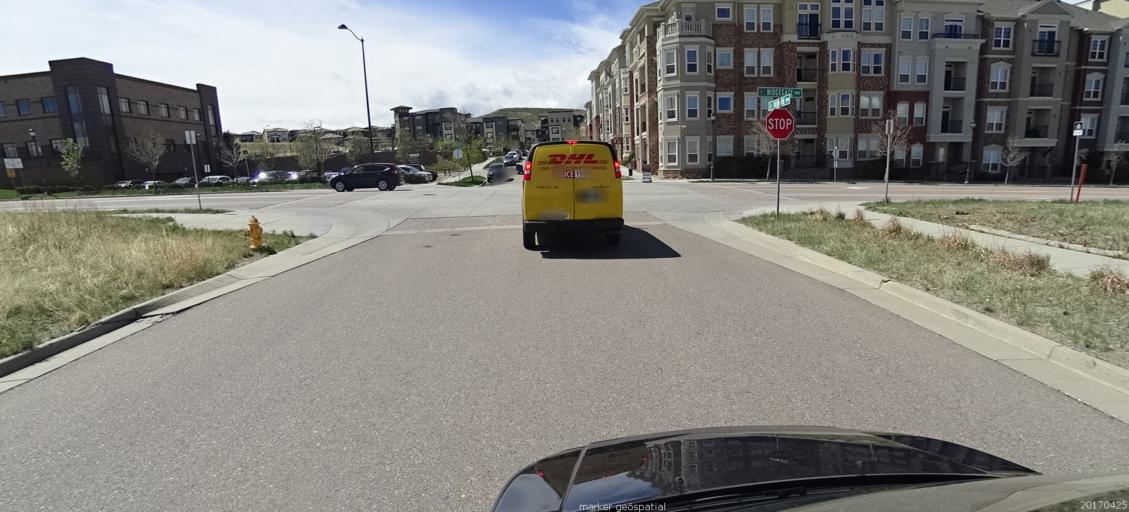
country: US
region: Colorado
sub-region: Adams County
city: Lone Tree
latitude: 39.5302
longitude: -104.8757
